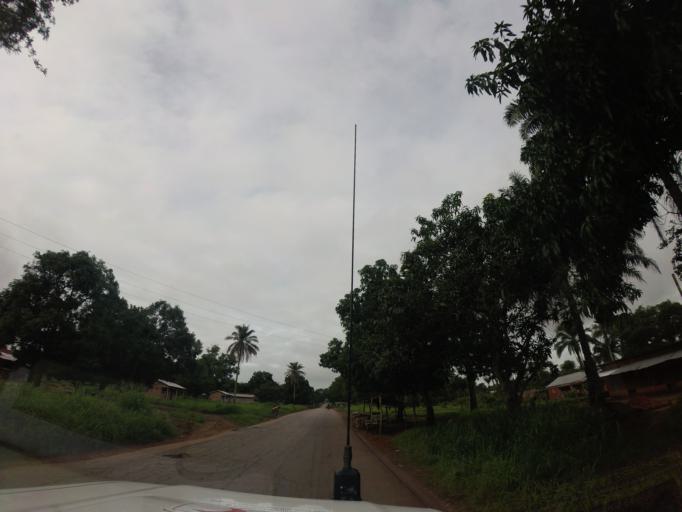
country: GN
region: Kindia
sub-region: Kindia
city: Kindia
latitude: 9.9860
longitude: -12.9120
